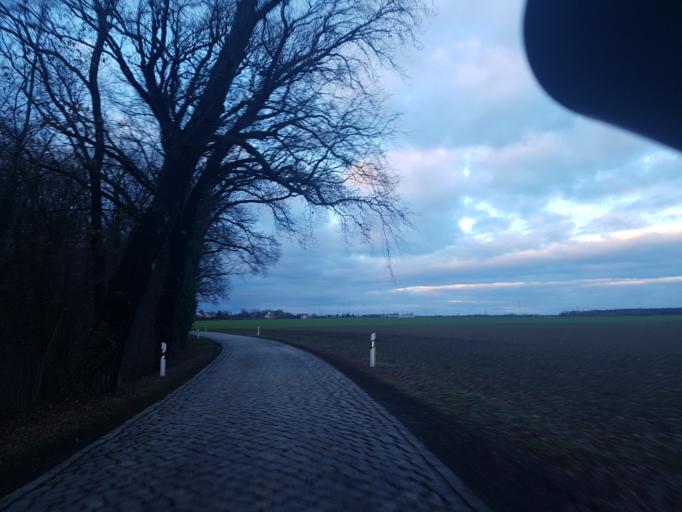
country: DE
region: Brandenburg
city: Muhlberg
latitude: 51.4655
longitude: 13.2057
